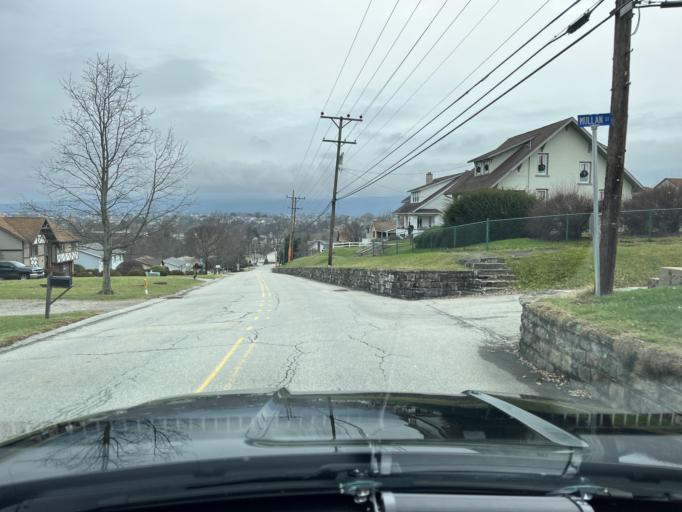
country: US
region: Pennsylvania
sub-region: Fayette County
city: South Uniontown
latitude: 39.8953
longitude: -79.7465
